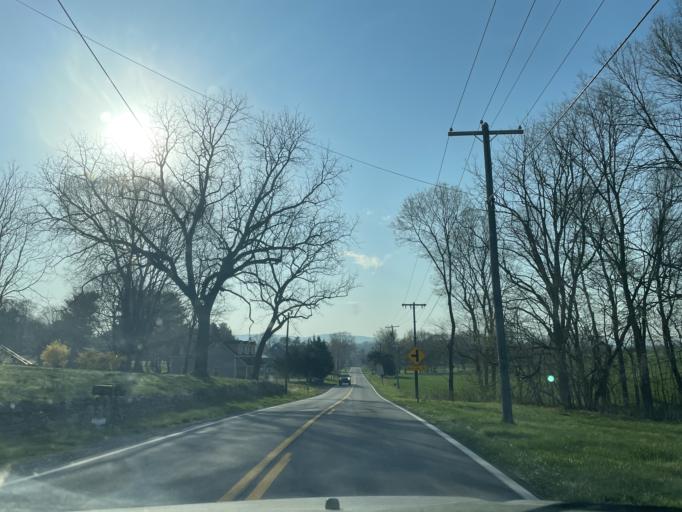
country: US
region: Maryland
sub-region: Washington County
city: Saint James
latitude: 39.5449
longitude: -77.7199
